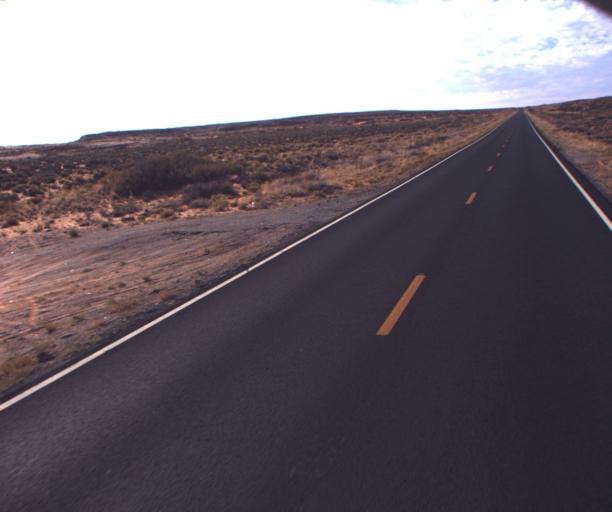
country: US
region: Arizona
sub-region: Apache County
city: Many Farms
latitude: 36.9089
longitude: -109.6239
